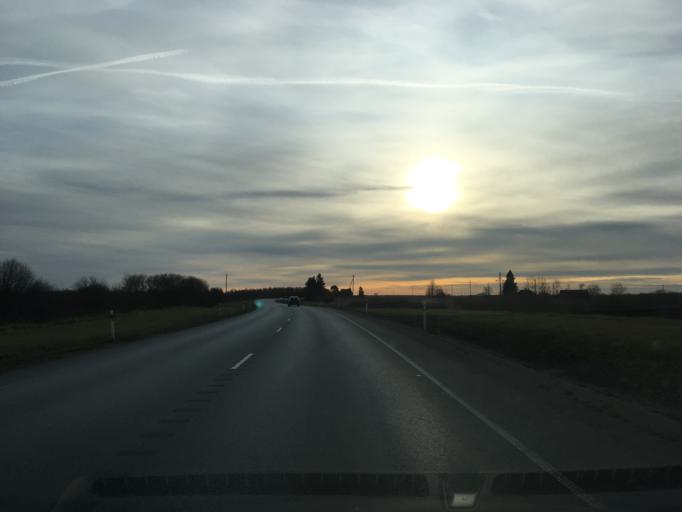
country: EE
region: Ida-Virumaa
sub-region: Kivioli linn
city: Kivioli
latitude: 59.4237
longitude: 26.9642
